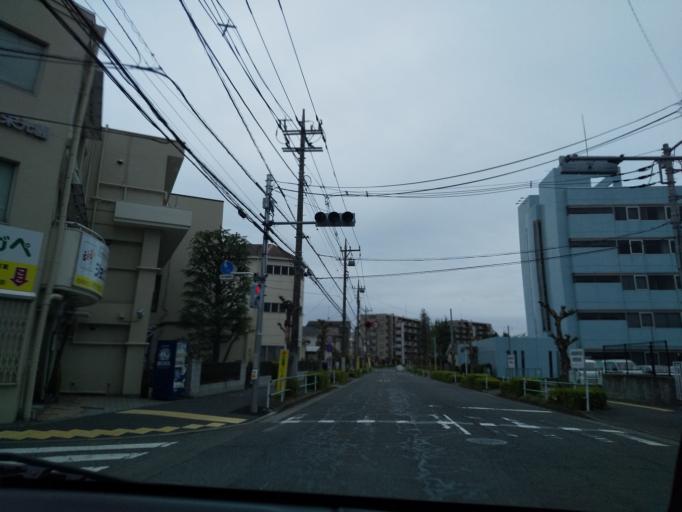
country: JP
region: Tokyo
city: Hino
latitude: 35.6566
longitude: 139.3721
